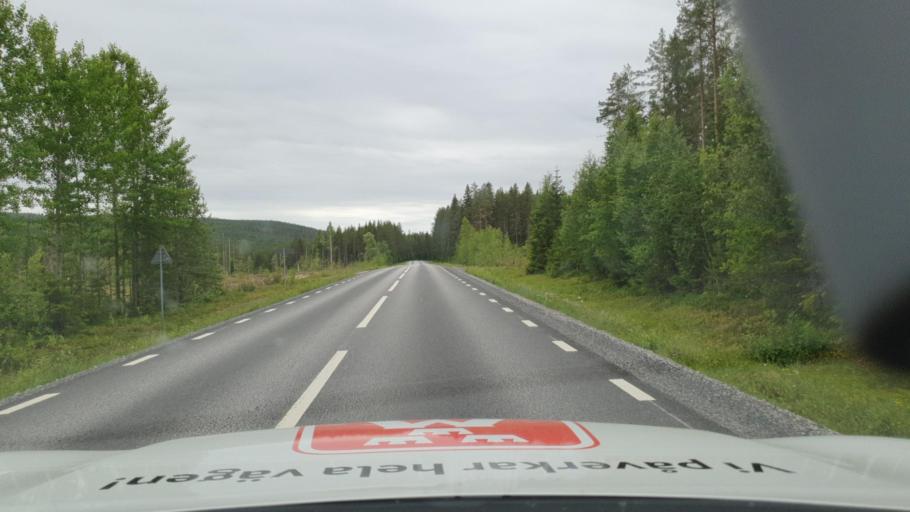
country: SE
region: Vaesterbotten
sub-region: Vannas Kommun
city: Vaennaes
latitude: 63.7307
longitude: 19.6521
